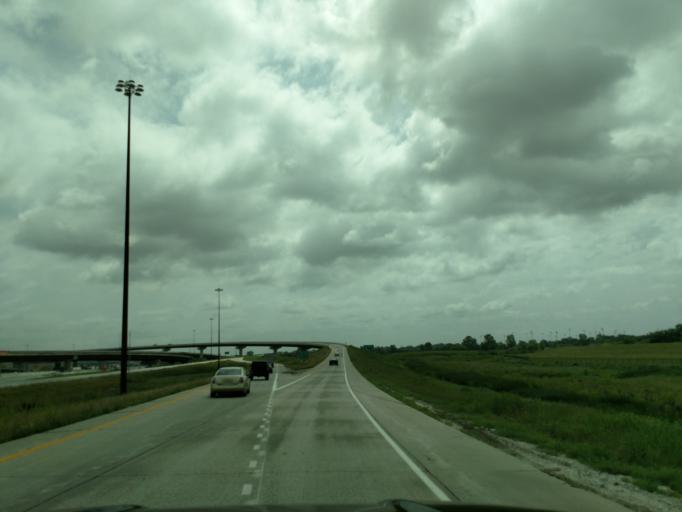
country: US
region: Nebraska
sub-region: Douglas County
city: Omaha
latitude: 41.2318
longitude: -95.9031
